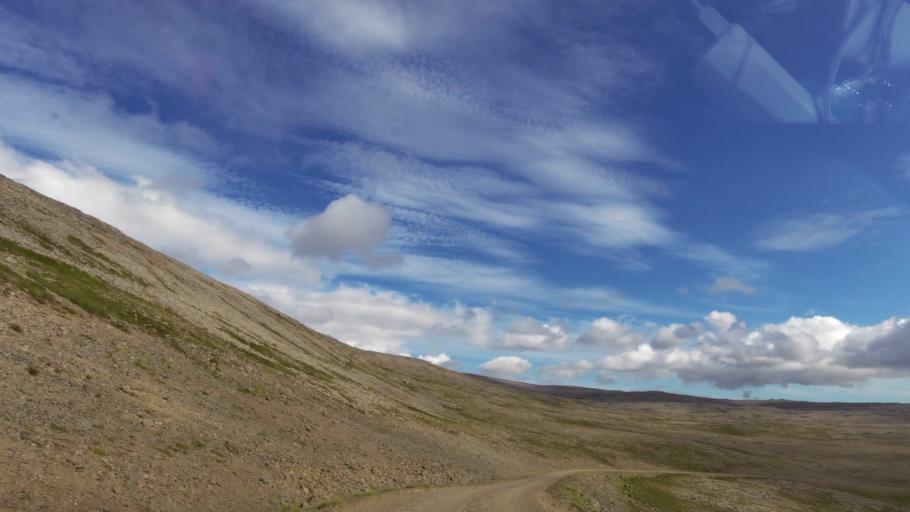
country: IS
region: West
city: Olafsvik
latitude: 65.6171
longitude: -24.3072
